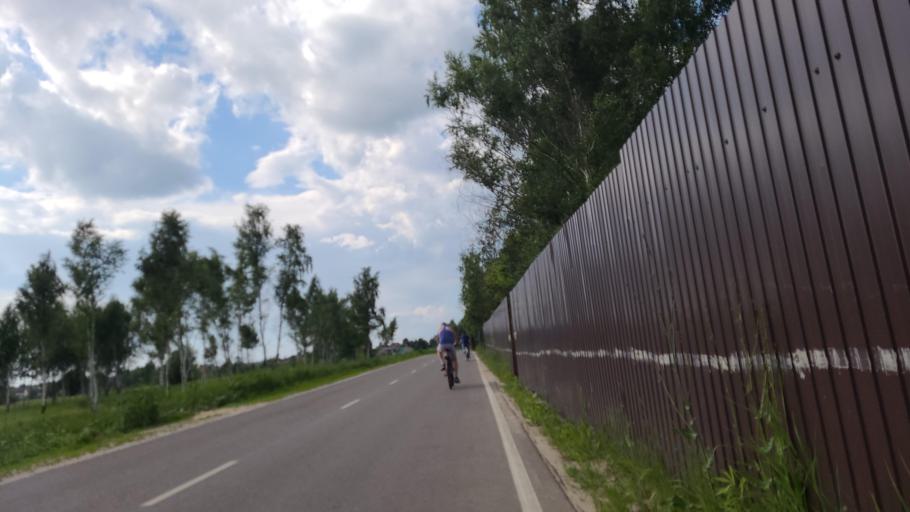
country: RU
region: Moskovskaya
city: Konobeyevo
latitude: 55.3999
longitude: 38.6782
